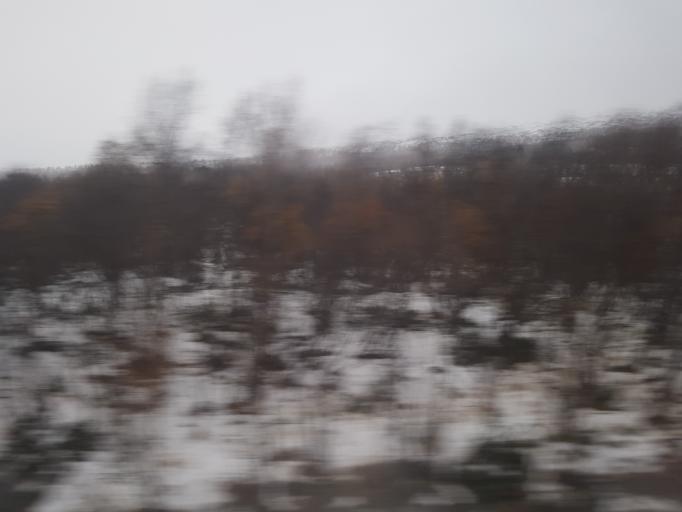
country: NO
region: Oppland
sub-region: Dovre
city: Dovre
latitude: 62.1740
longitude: 9.4465
